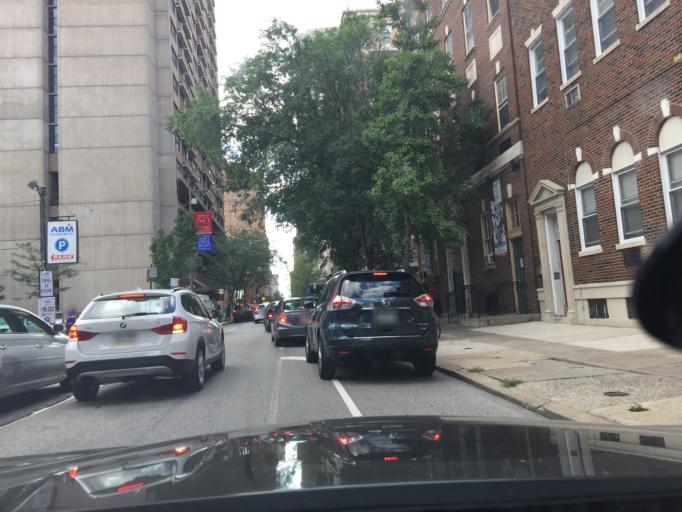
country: US
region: Pennsylvania
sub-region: Philadelphia County
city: Philadelphia
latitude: 39.9468
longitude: -75.1630
